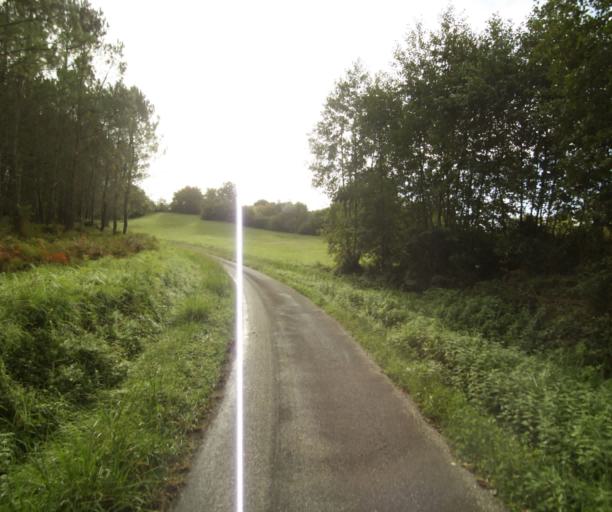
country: FR
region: Midi-Pyrenees
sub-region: Departement du Gers
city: Nogaro
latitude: 43.8228
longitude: -0.0801
